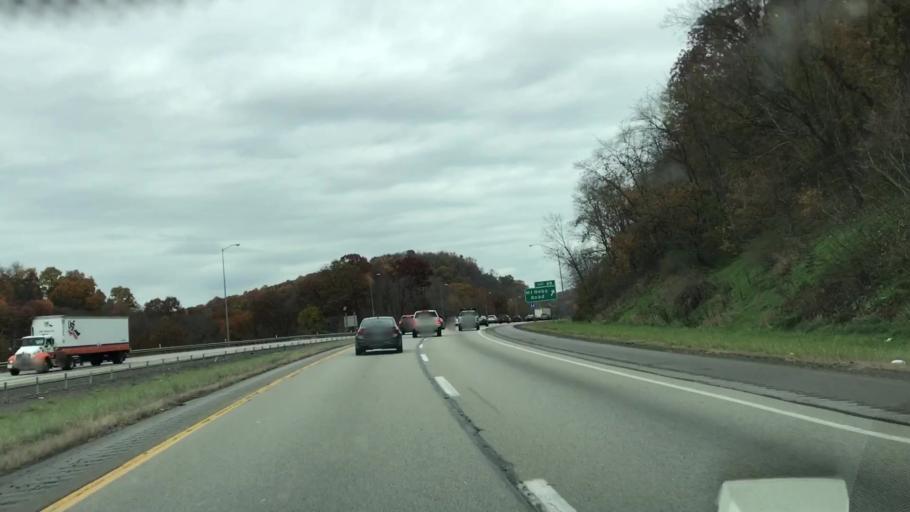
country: US
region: Pennsylvania
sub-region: Allegheny County
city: Emsworth
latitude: 40.5465
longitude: -80.1218
